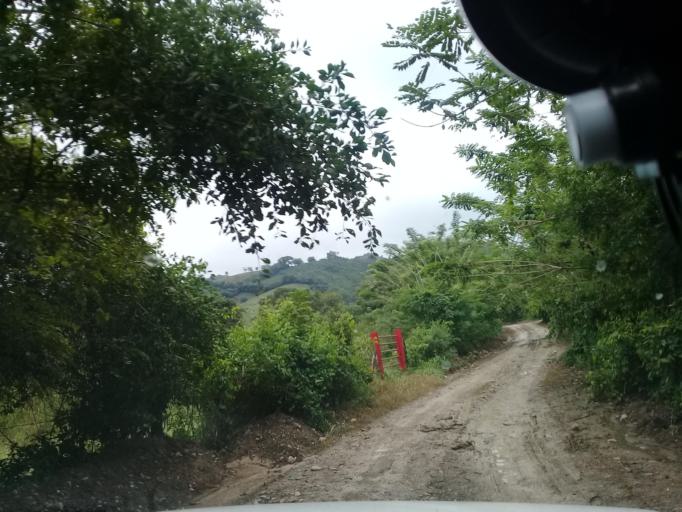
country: MX
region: Veracruz
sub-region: Chalma
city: San Pedro Coyutla
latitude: 21.2377
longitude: -98.4184
